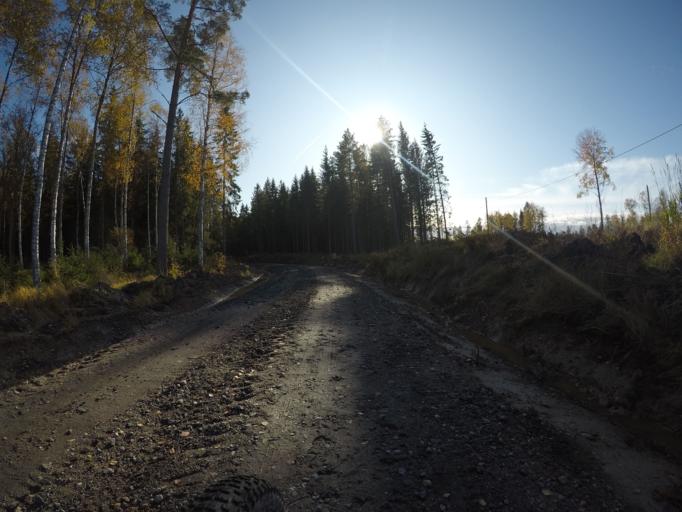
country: SE
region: Vaestmanland
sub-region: Kungsors Kommun
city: Kungsoer
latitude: 59.3110
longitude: 16.0980
